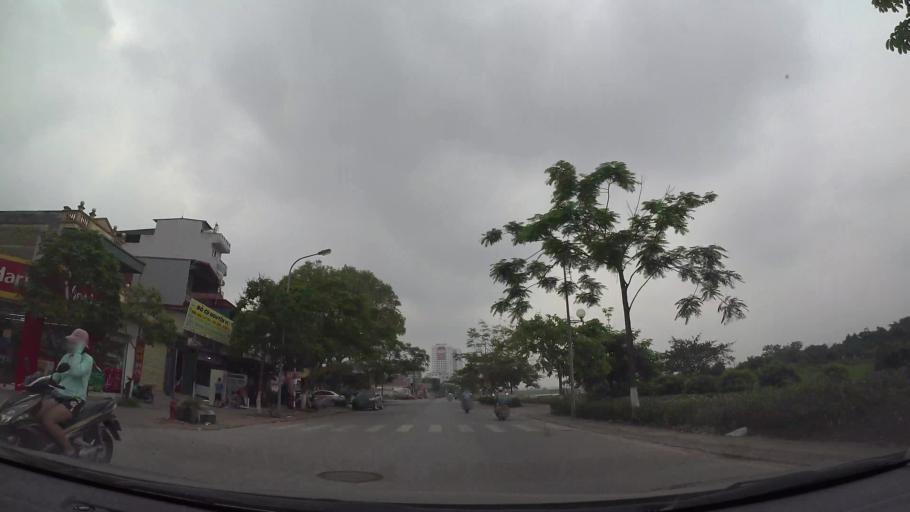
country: VN
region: Ha Noi
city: Trau Quy
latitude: 21.0400
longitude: 105.9280
